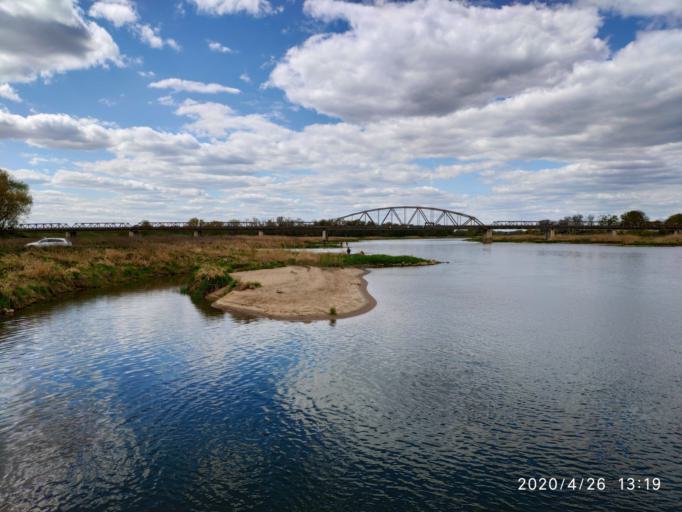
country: PL
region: Lubusz
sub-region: Powiat zielonogorski
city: Sulechow
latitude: 52.0298
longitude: 15.6181
